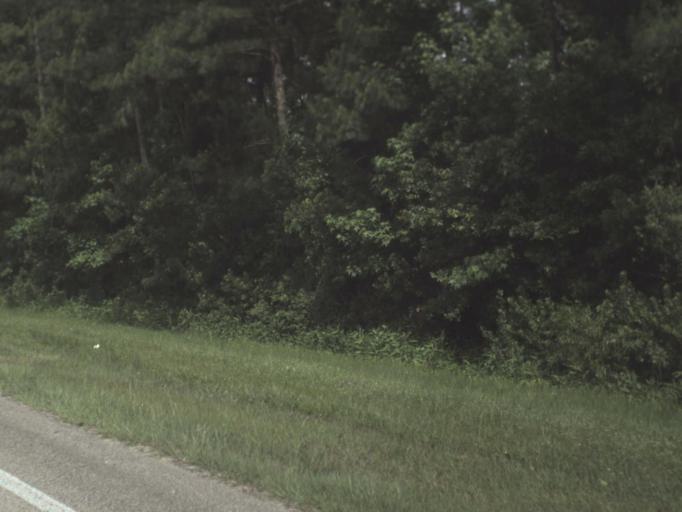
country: US
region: Florida
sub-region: Clay County
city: Middleburg
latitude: 30.0888
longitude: -81.8542
